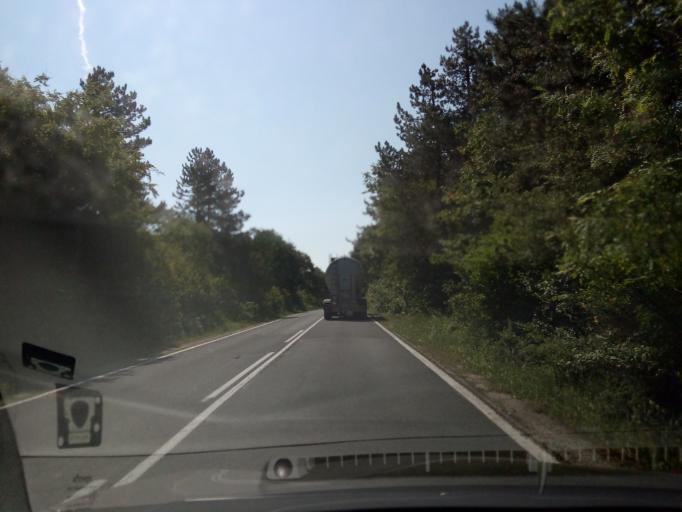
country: BG
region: Burgas
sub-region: Obshtina Nesebur
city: Sveti Vlas
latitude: 42.7737
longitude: 27.7753
